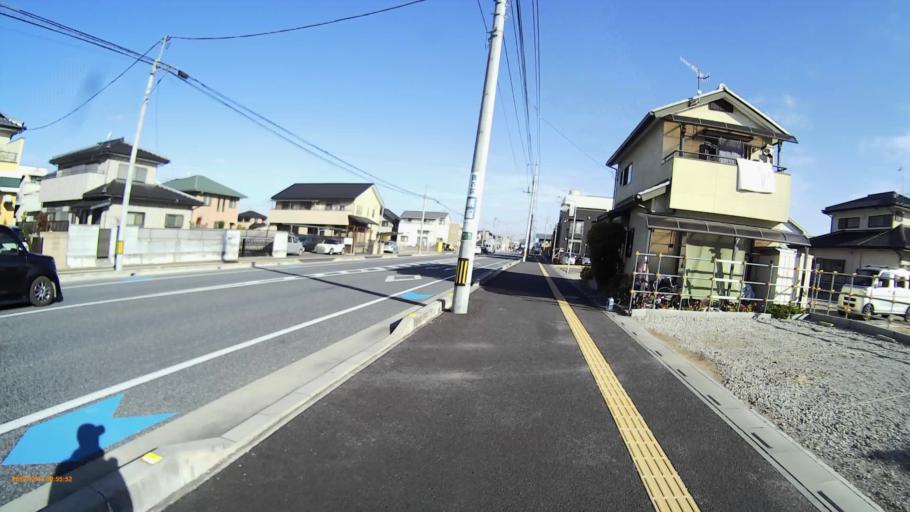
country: JP
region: Saitama
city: Fukayacho
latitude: 36.1764
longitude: 139.3321
